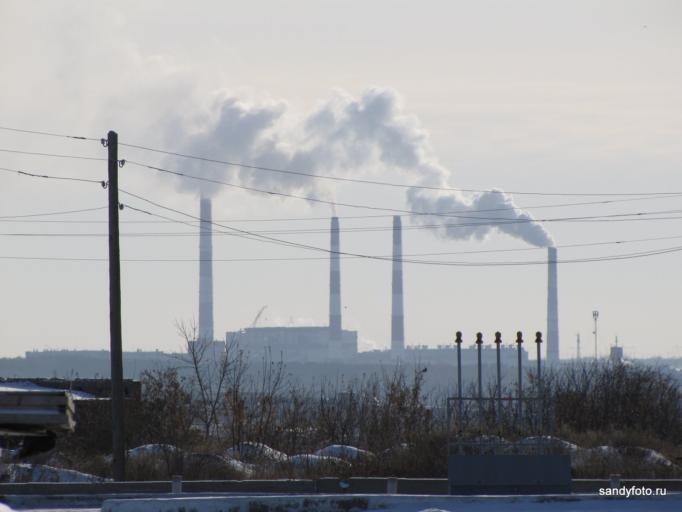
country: RU
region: Chelyabinsk
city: Troitsk
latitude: 54.1038
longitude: 61.5752
